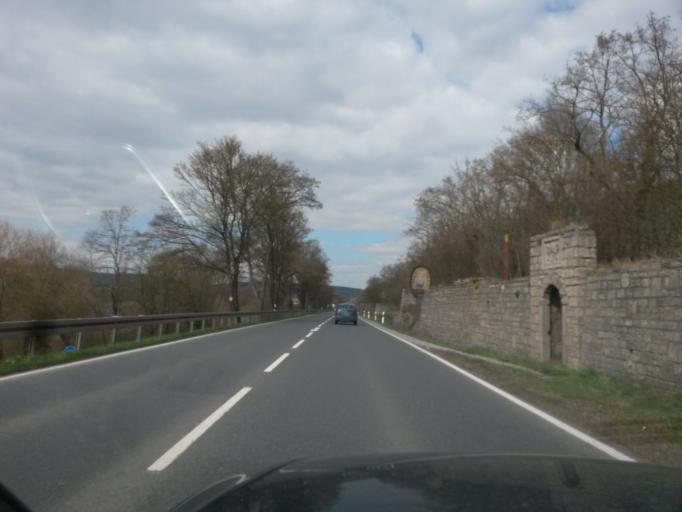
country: DE
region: Bavaria
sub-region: Regierungsbezirk Unterfranken
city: Randersacker
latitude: 49.7623
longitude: 9.9739
